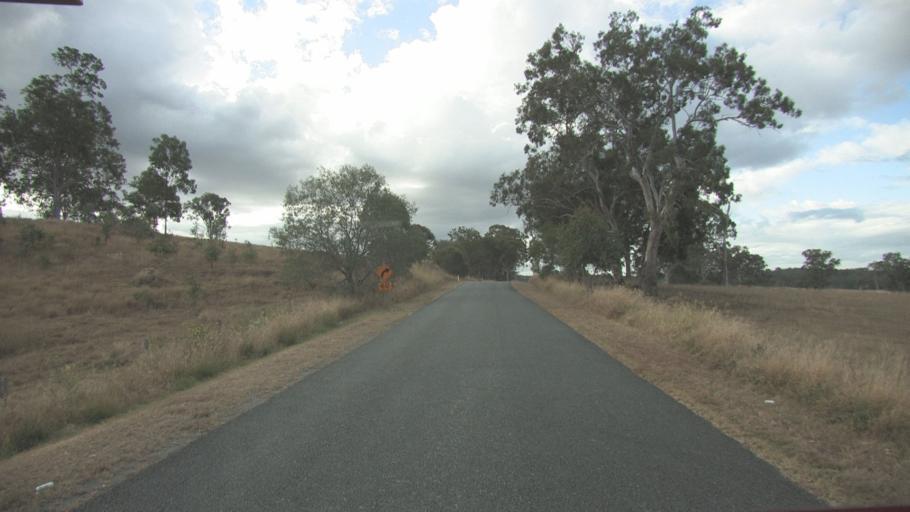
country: AU
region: Queensland
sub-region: Logan
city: Cedar Vale
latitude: -27.8925
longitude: 153.0655
